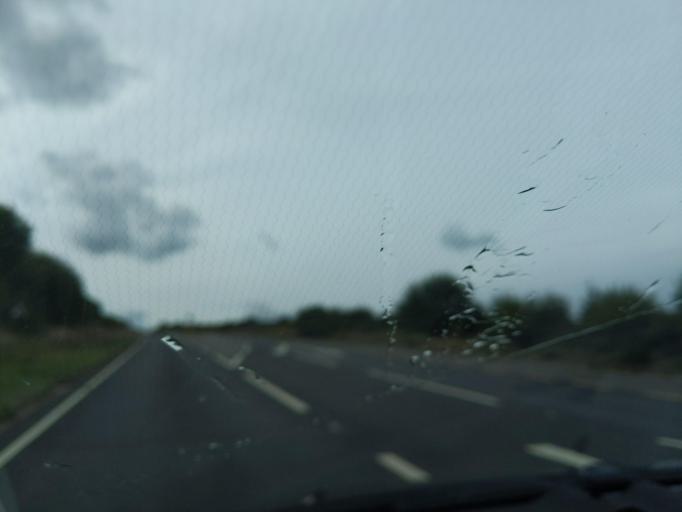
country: GB
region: England
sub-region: Cornwall
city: Liskeard
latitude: 50.4531
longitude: -4.5336
